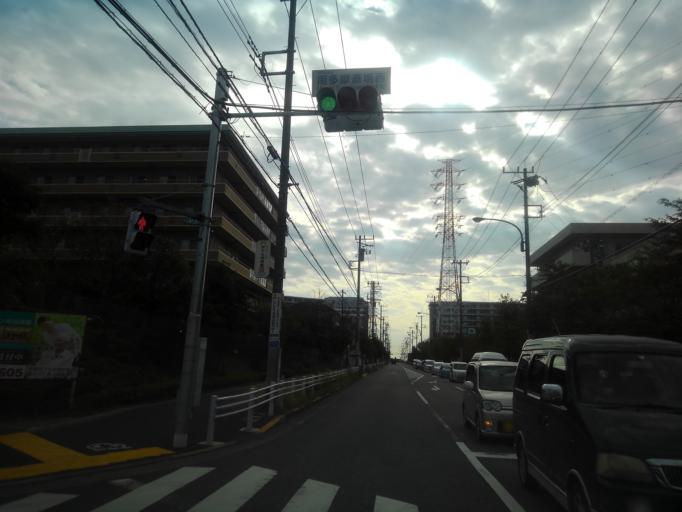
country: JP
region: Tokyo
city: Hino
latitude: 35.5986
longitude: 139.3827
